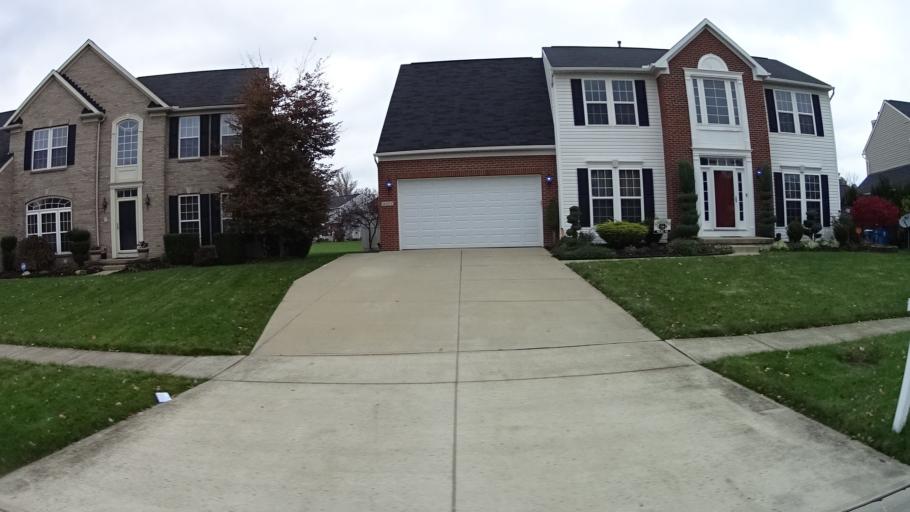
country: US
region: Ohio
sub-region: Lorain County
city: Amherst
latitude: 41.4318
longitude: -82.2253
